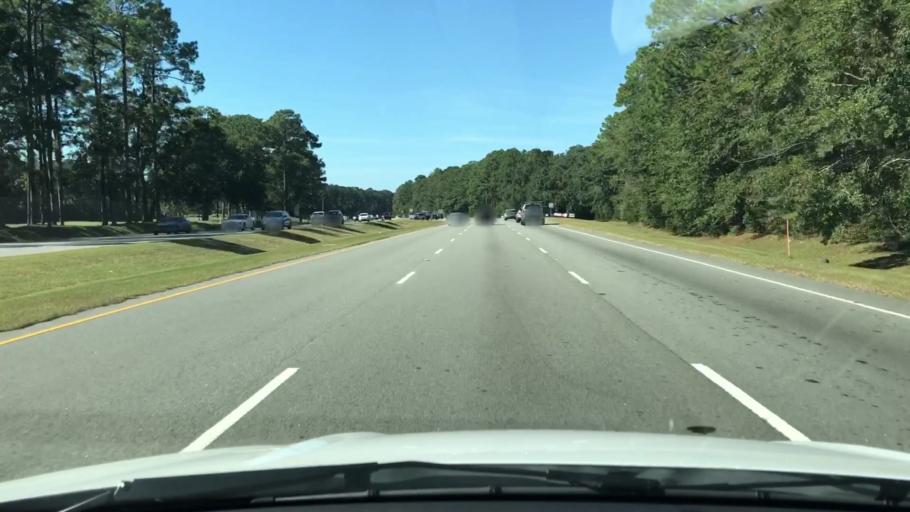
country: US
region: South Carolina
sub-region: Beaufort County
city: Bluffton
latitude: 32.2853
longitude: -80.8855
